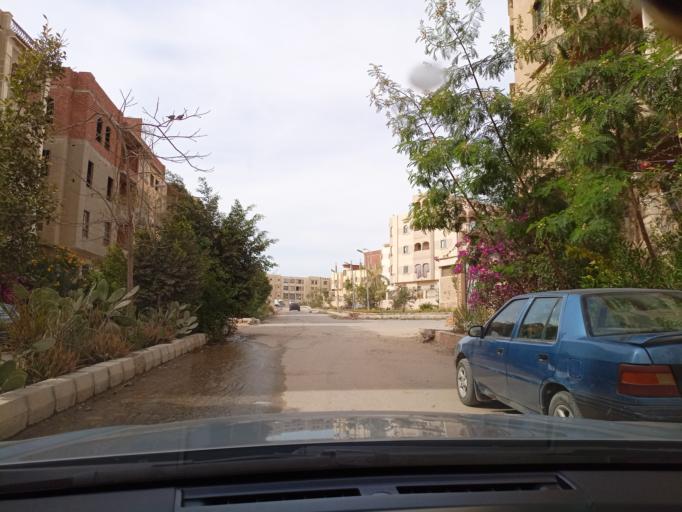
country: EG
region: Muhafazat al Qalyubiyah
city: Al Khankah
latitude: 30.2593
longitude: 31.4785
